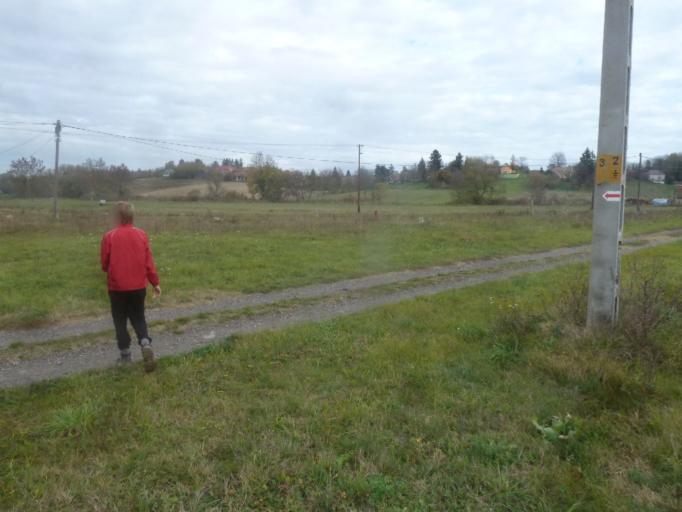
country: HU
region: Zala
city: Pacsa
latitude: 46.6170
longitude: 17.0447
